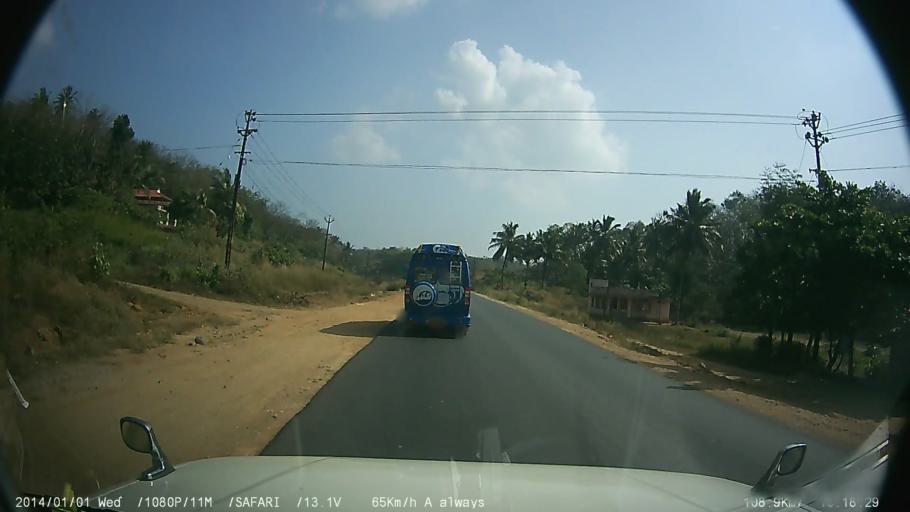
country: IN
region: Kerala
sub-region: Thrissur District
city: Chelakara
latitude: 10.5909
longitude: 76.4581
